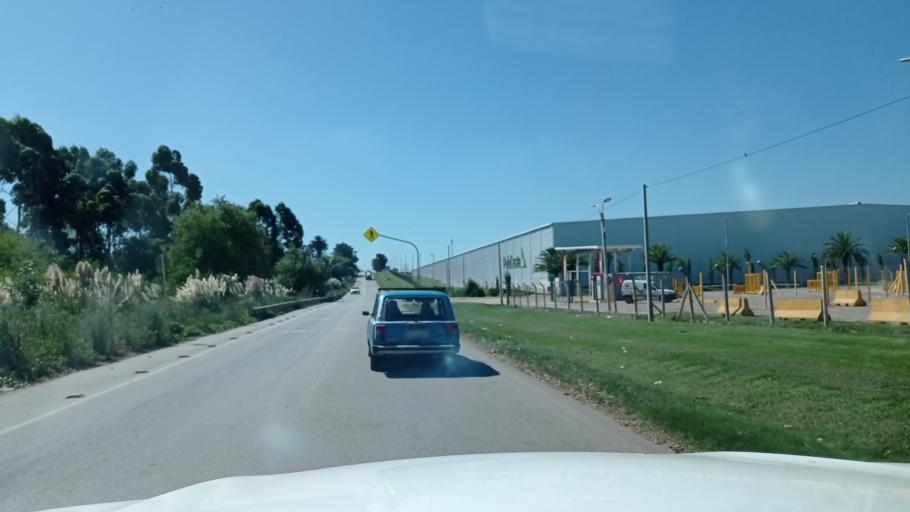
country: UY
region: Montevideo
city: Pajas Blancas
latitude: -34.8596
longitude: -56.2888
